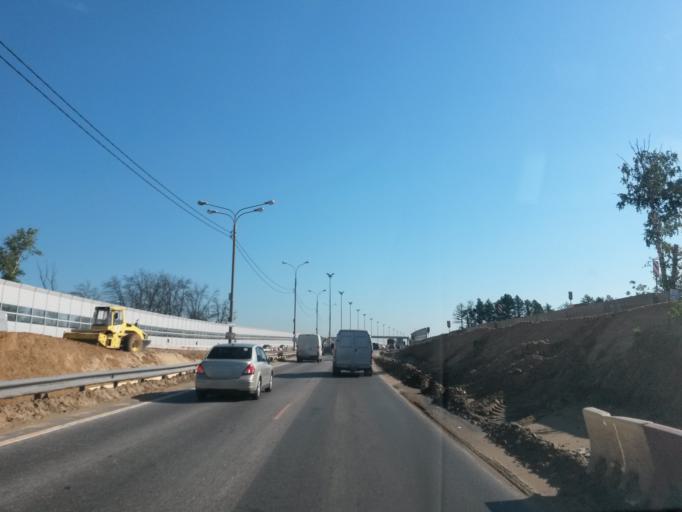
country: RU
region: Moskovskaya
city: Lesnyye Polyany
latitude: 55.9673
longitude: 37.8423
